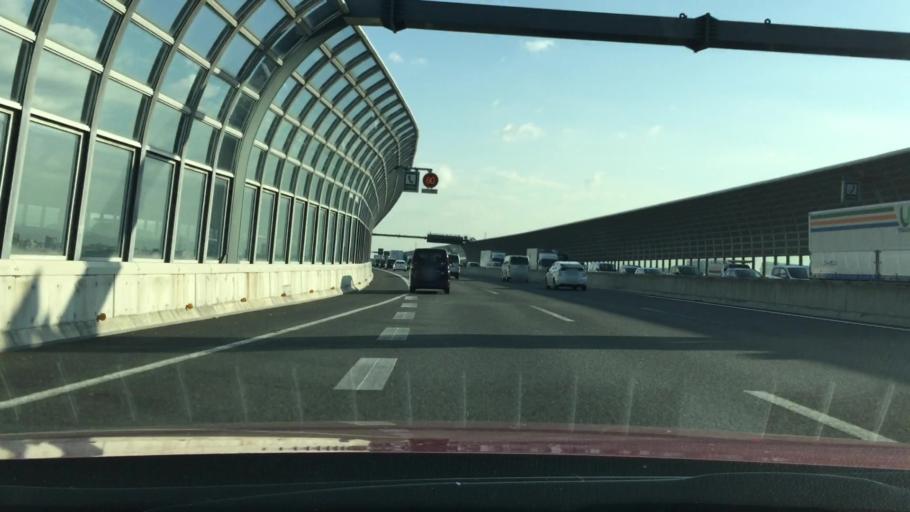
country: JP
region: Osaka
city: Daitocho
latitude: 34.7215
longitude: 135.5992
